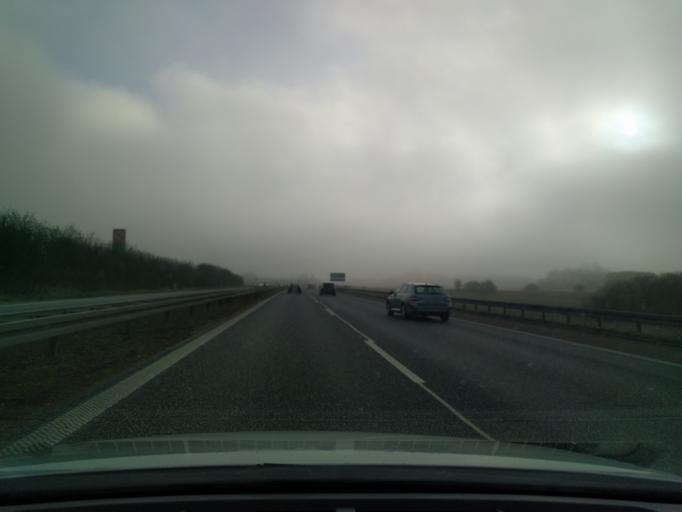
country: DK
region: Zealand
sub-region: Soro Kommune
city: Soro
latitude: 55.4578
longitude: 11.5709
